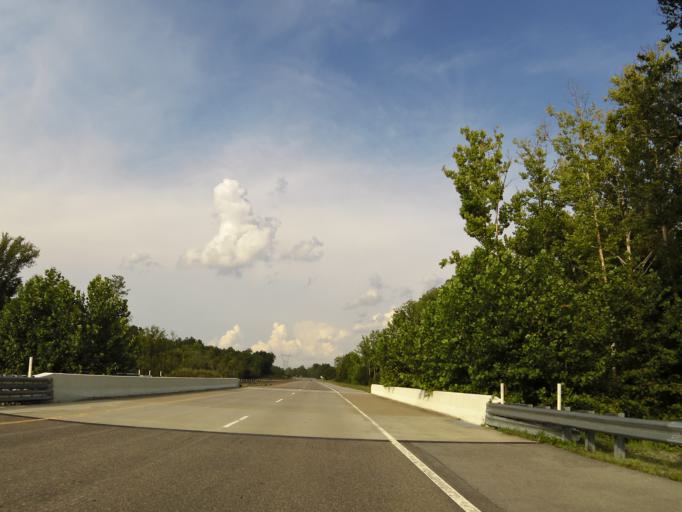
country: US
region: Tennessee
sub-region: Roane County
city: Oliver Springs
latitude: 35.9697
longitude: -84.3467
